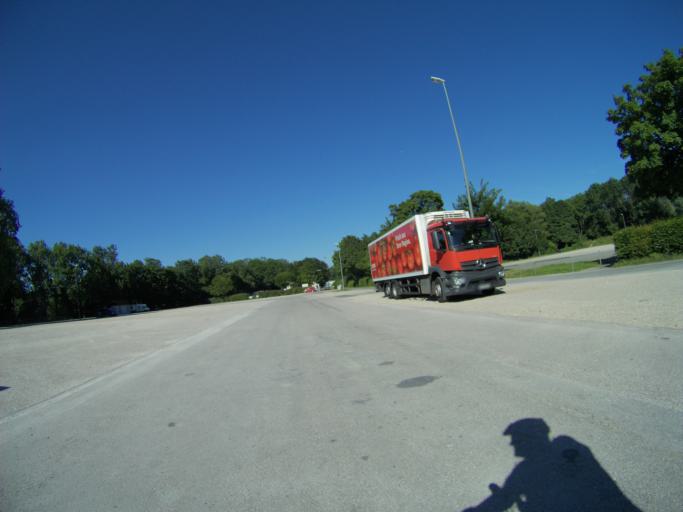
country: DE
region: Bavaria
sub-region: Upper Bavaria
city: Freising
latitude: 48.4011
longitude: 11.7555
